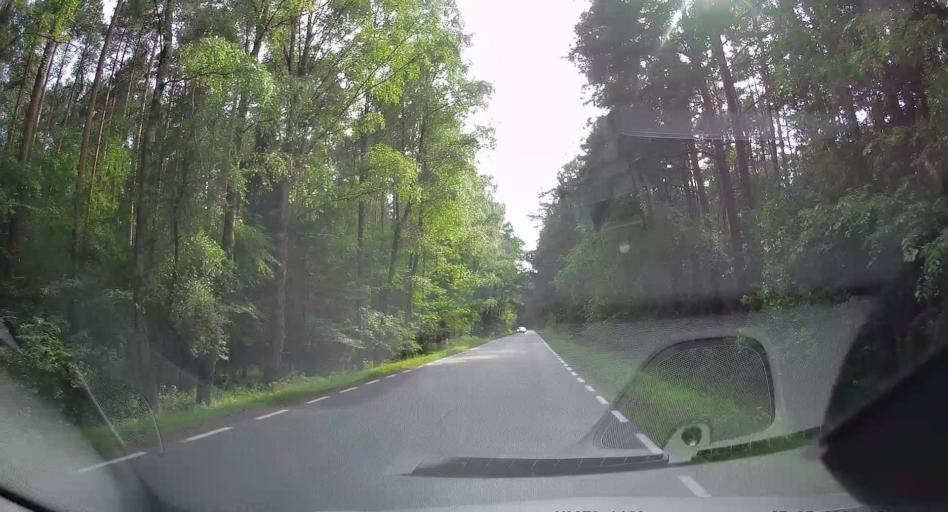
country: PL
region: Lodz Voivodeship
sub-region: Powiat tomaszowski
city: Inowlodz
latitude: 51.5480
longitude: 20.2414
